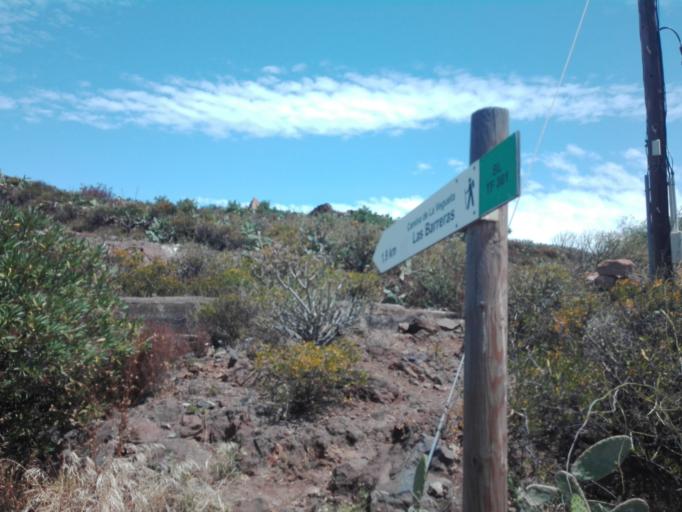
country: ES
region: Canary Islands
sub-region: Provincia de Santa Cruz de Tenerife
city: Candelaria
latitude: 28.4117
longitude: -16.3482
